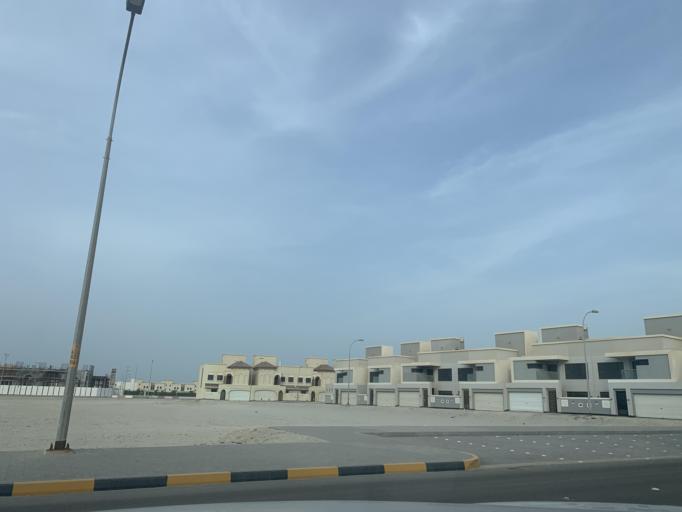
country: BH
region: Muharraq
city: Al Muharraq
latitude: 26.3160
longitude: 50.6224
